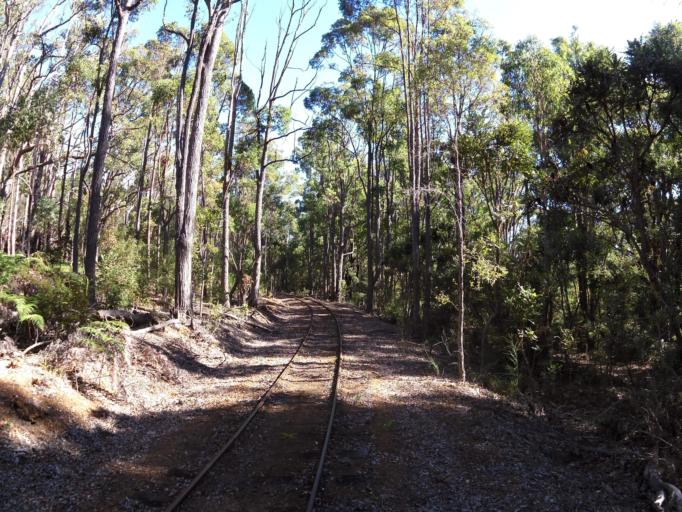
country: AU
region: Western Australia
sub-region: Waroona
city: Waroona
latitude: -32.7103
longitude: 116.0785
